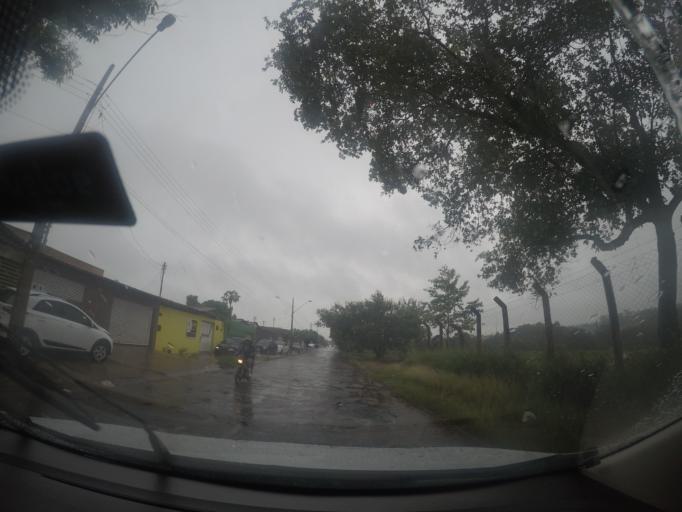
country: BR
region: Goias
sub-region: Goiania
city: Goiania
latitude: -16.6036
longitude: -49.3490
